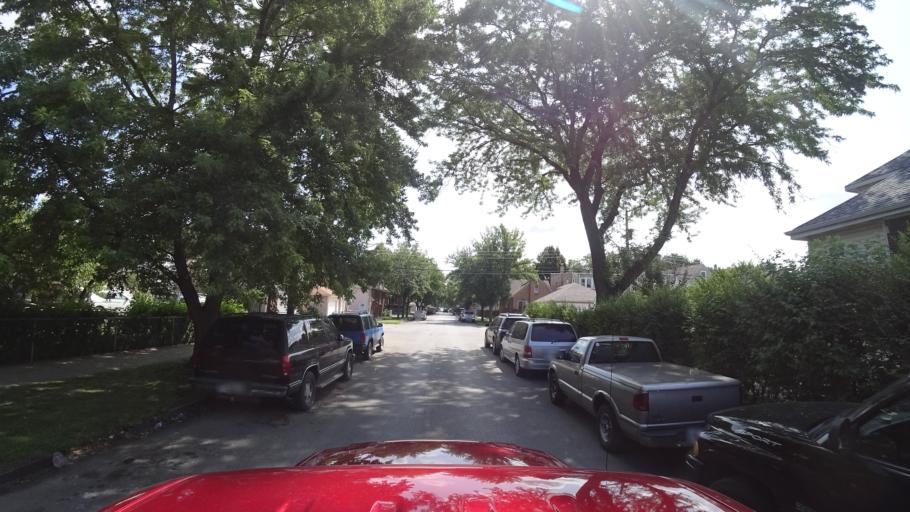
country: US
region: Illinois
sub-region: Cook County
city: Cicero
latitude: 41.8350
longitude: -87.7278
